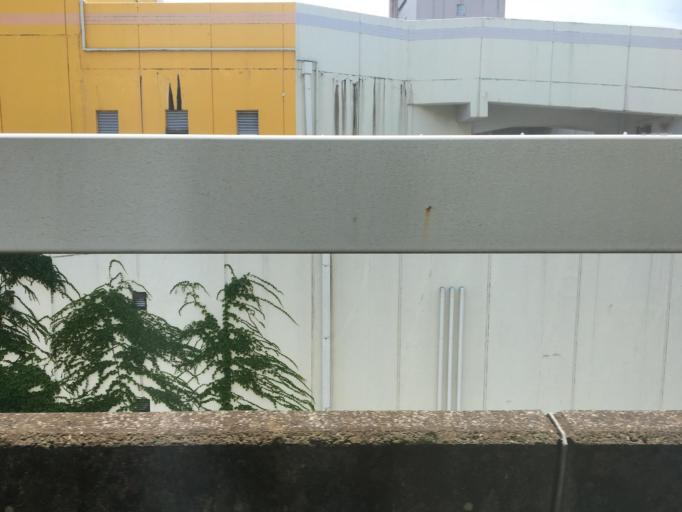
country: JP
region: Gunma
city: Ota
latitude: 36.2936
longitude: 139.3786
